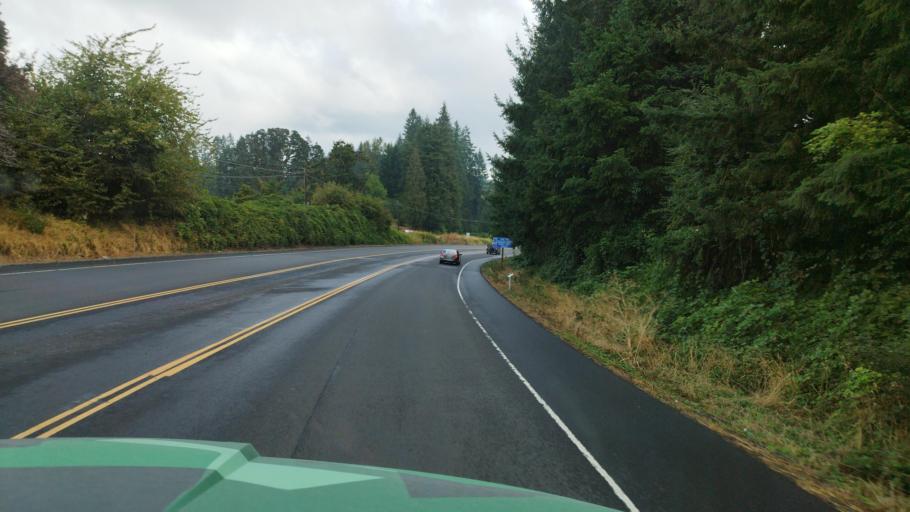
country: US
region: Oregon
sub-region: Yamhill County
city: Lafayette
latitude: 45.2454
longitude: -123.1254
